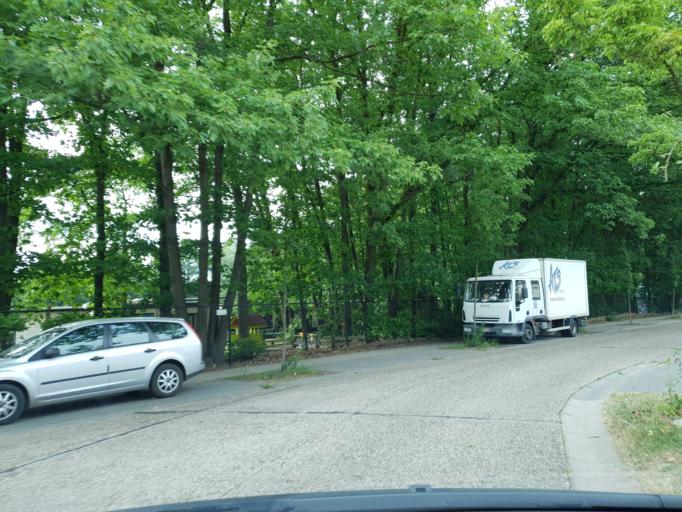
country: BE
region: Flanders
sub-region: Provincie Antwerpen
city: Brasschaat
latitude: 51.3002
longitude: 4.5100
